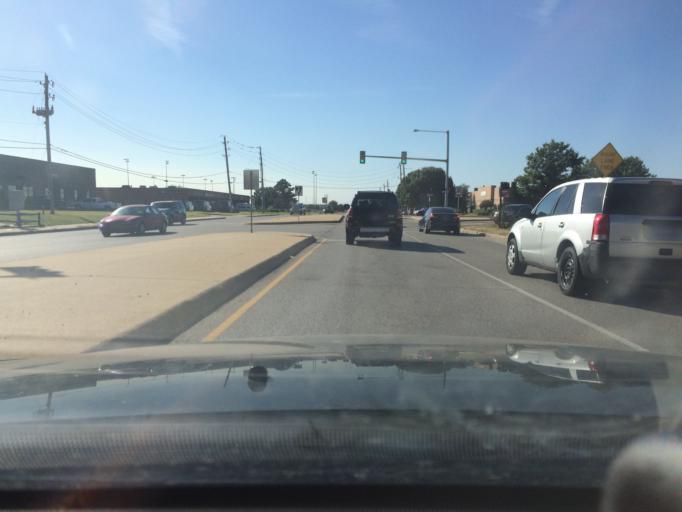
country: US
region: Oklahoma
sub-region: Tulsa County
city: Broken Arrow
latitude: 36.0900
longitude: -95.8380
